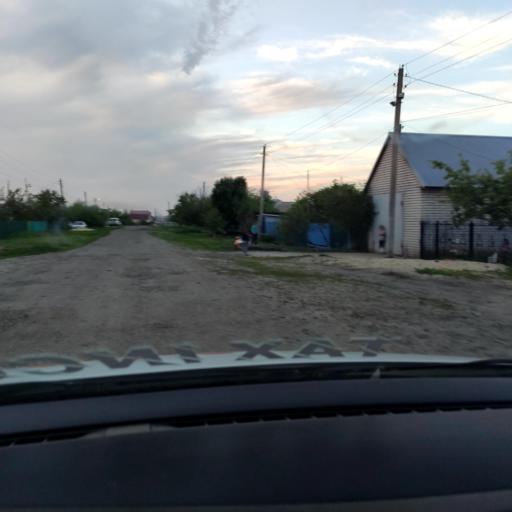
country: RU
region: Voronezj
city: Maslovka
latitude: 51.4544
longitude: 39.2378
